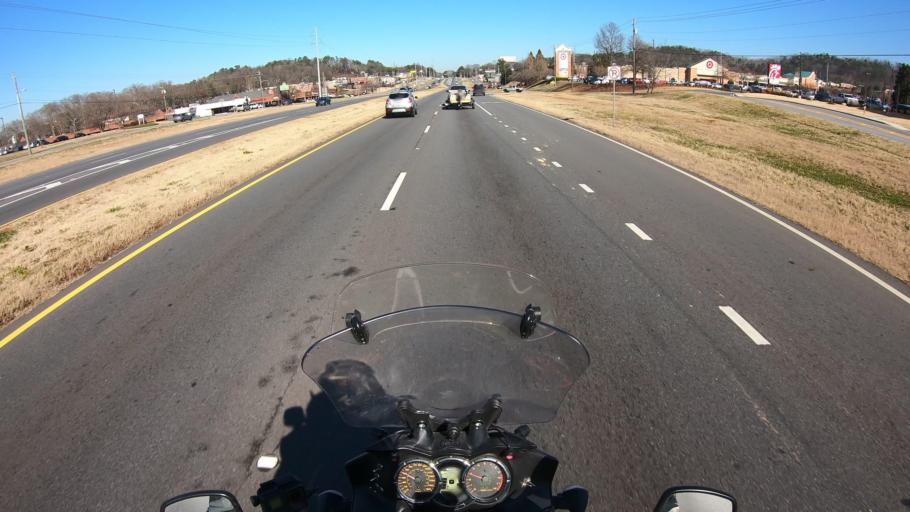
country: US
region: Georgia
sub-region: Bartow County
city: Cartersville
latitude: 34.1708
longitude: -84.7860
